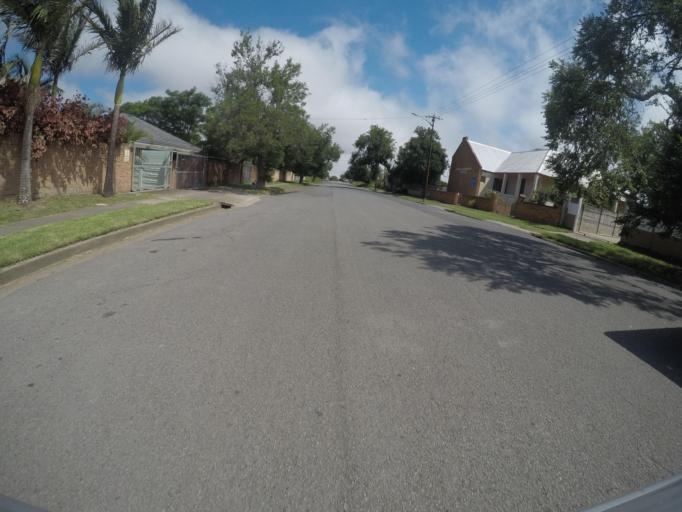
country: ZA
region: Eastern Cape
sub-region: Buffalo City Metropolitan Municipality
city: East London
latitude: -32.9769
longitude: 27.8896
